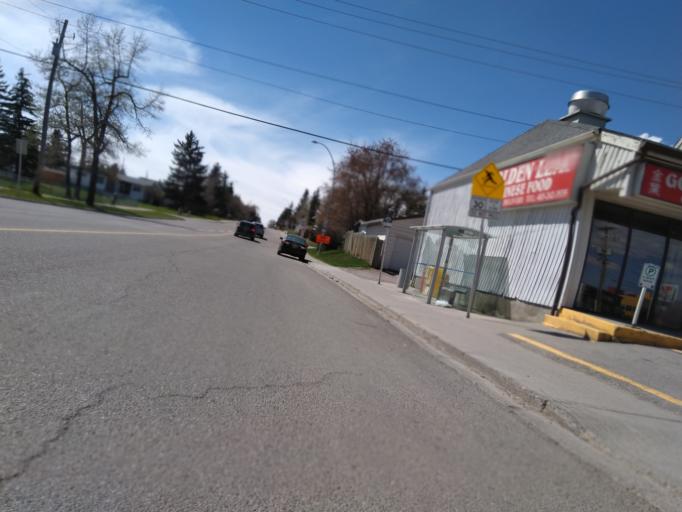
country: CA
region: Alberta
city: Calgary
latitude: 51.0125
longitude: -114.1415
